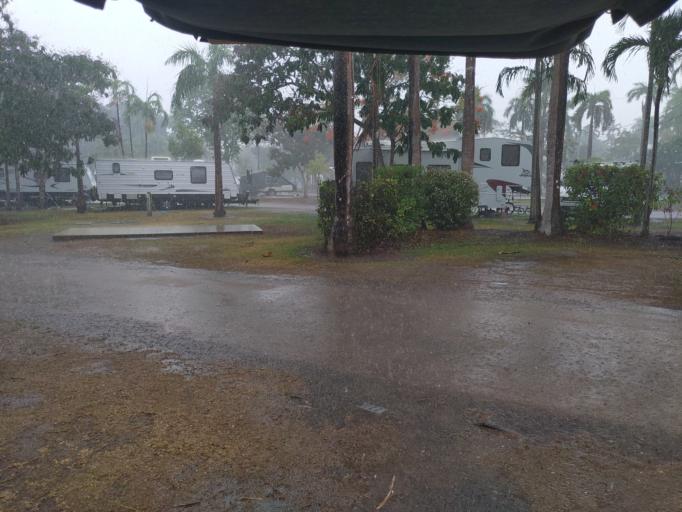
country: AU
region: Northern Territory
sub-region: Palmerston
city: Palmerston
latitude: -12.4579
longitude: 130.9726
